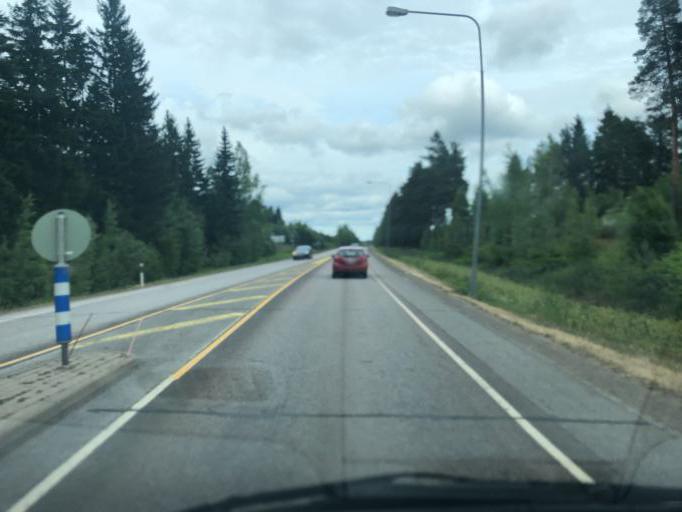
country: FI
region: Kymenlaakso
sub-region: Kouvola
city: Kouvola
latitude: 60.9132
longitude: 26.7699
